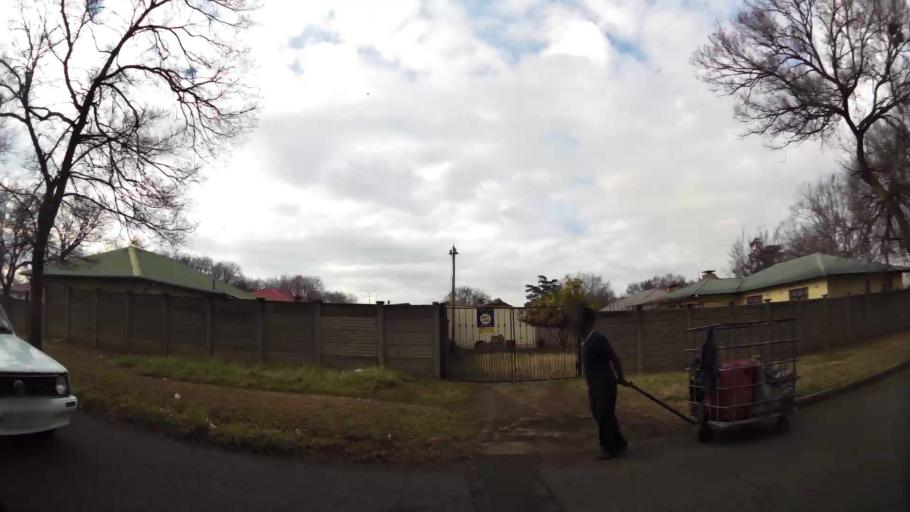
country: ZA
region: Gauteng
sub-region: Sedibeng District Municipality
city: Vanderbijlpark
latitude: -26.6914
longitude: 27.8203
